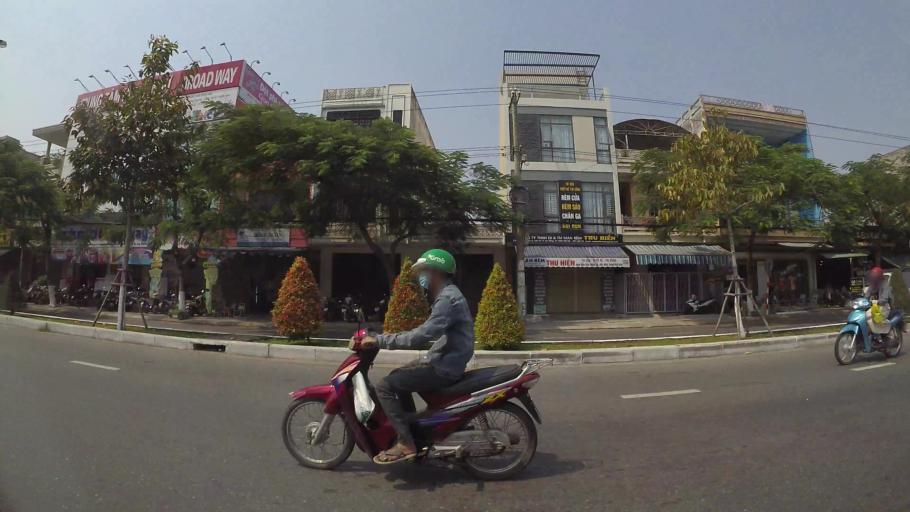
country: VN
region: Da Nang
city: Son Tra
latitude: 16.0458
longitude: 108.2391
